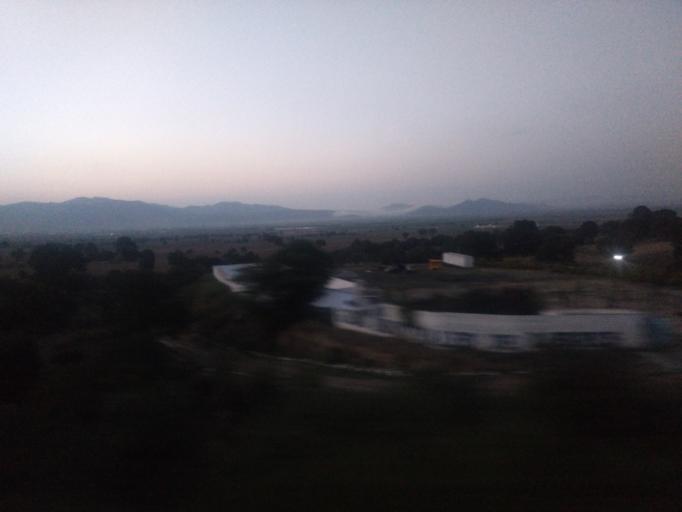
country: MX
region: Puebla
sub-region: Oriental
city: San Antonio Virreyes
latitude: 19.4105
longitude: -97.6547
